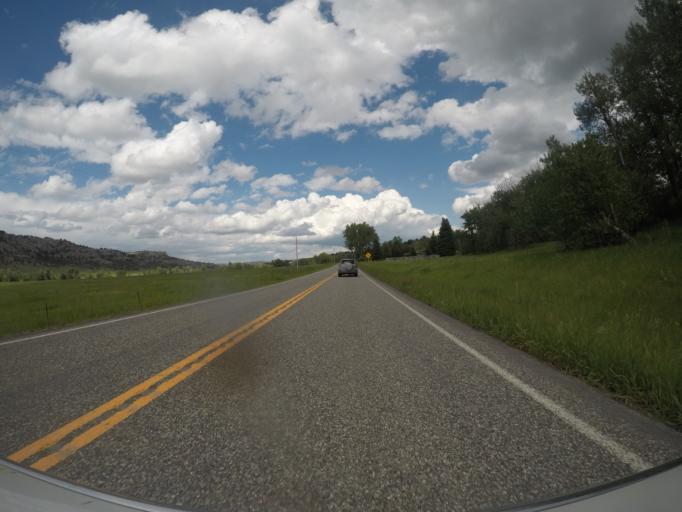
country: US
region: Montana
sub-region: Sweet Grass County
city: Big Timber
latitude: 45.6940
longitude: -110.0364
